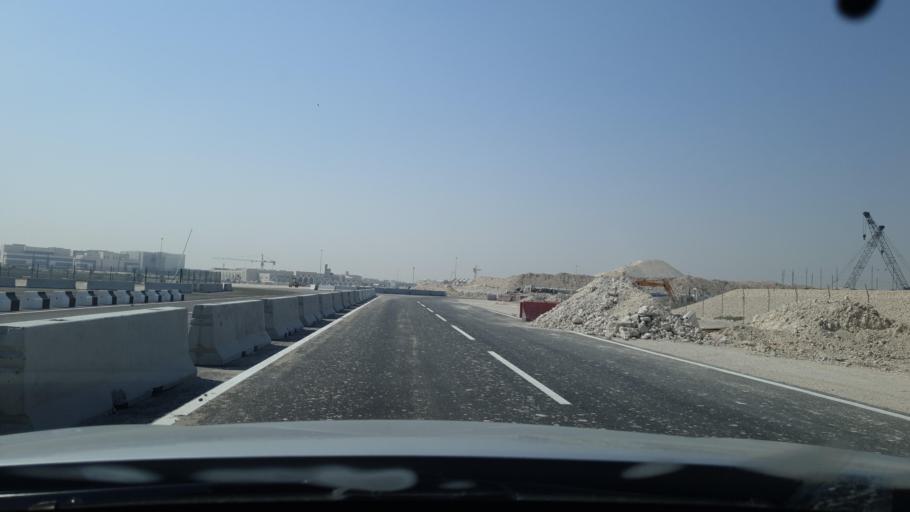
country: QA
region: Baladiyat ad Dawhah
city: Doha
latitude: 25.2242
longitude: 51.5262
